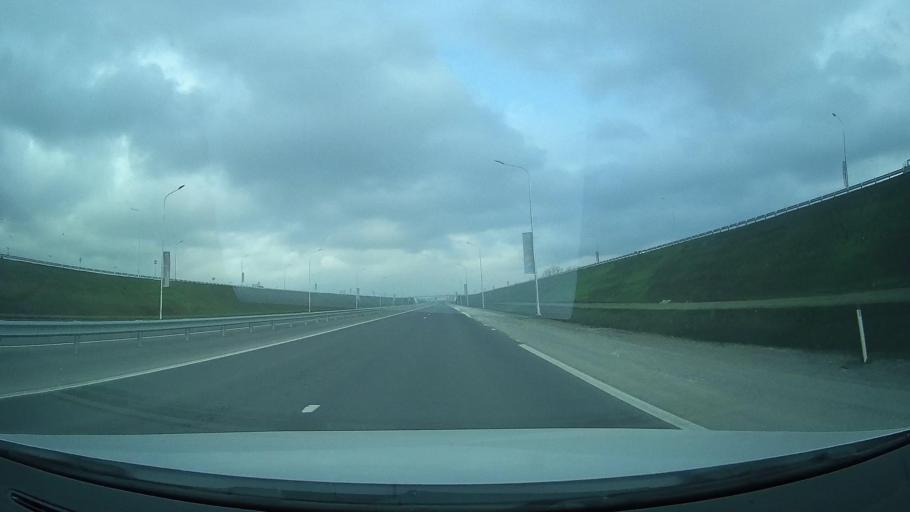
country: RU
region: Rostov
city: Grushevskaya
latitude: 47.4835
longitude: 39.9299
